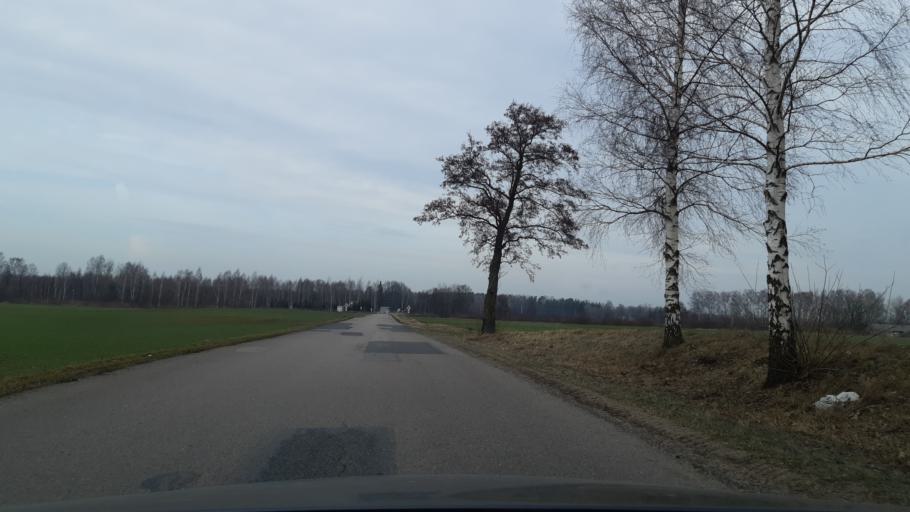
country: LT
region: Marijampoles apskritis
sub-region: Marijampole Municipality
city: Marijampole
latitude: 54.7238
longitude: 23.3370
